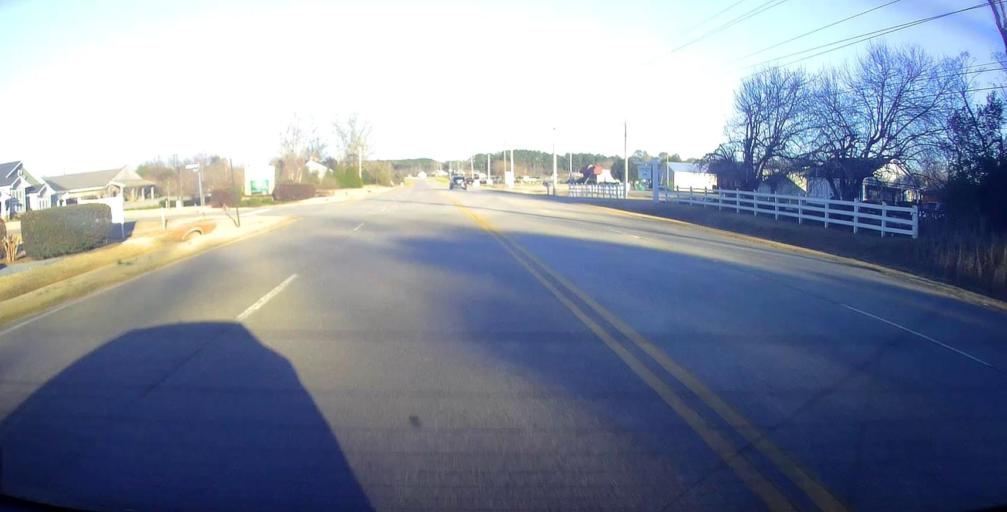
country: US
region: Georgia
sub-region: Dougherty County
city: Albany
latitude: 31.6295
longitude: -84.2353
